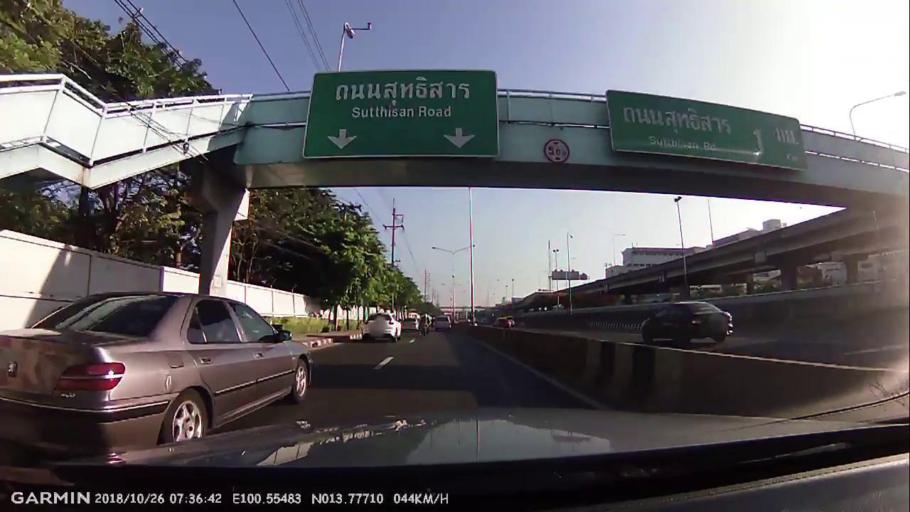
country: TH
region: Bangkok
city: Din Daeng
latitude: 13.7772
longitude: 100.5549
